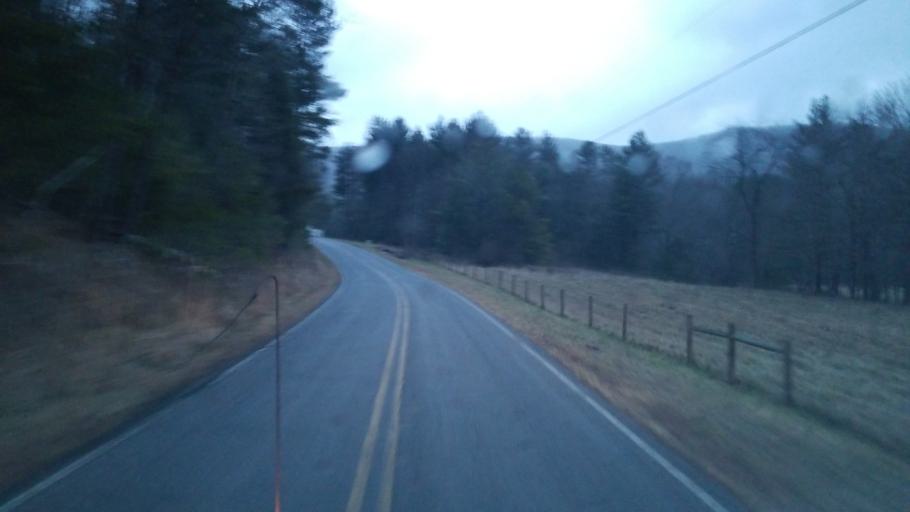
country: US
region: Virginia
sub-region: Pulaski County
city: Pulaski
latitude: 37.1149
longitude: -80.8812
